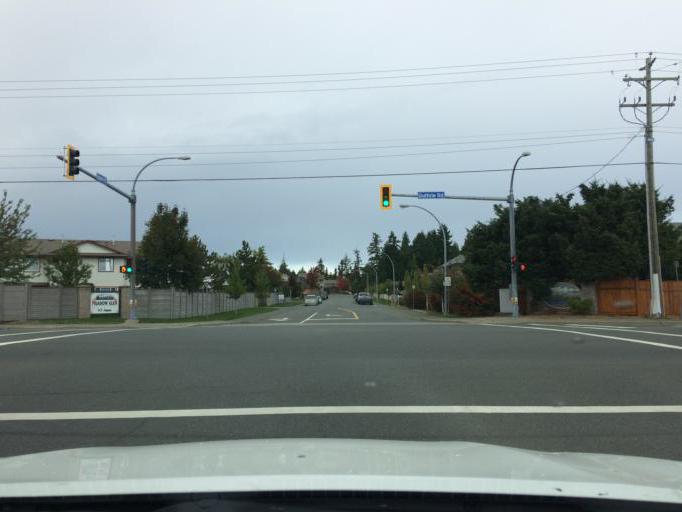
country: CA
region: British Columbia
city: Courtenay
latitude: 49.6882
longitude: -124.9432
